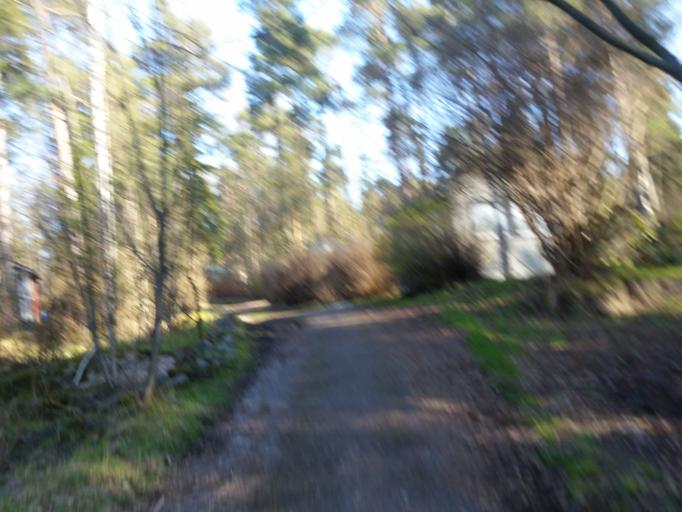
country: FI
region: Uusimaa
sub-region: Helsinki
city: Otaniemi
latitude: 60.1534
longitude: 24.8565
